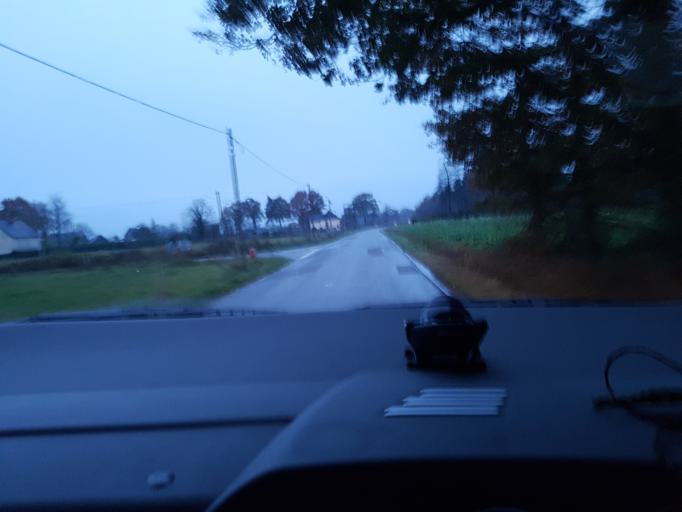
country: FR
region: Brittany
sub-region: Departement d'Ille-et-Vilaine
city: Montreuil-sous-Perouse
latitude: 48.1911
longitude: -1.2807
